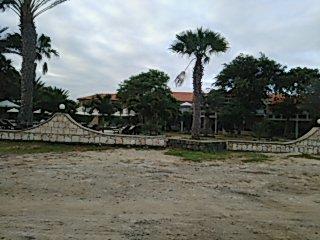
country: CV
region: Sal
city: Santa Maria
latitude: 16.5978
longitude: -22.9084
